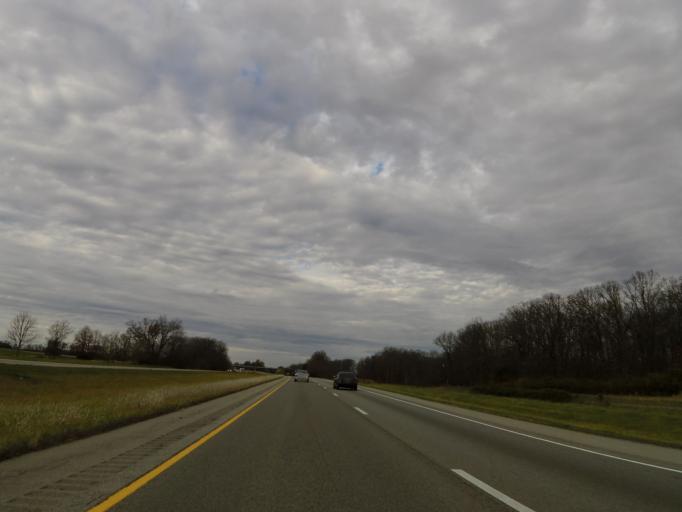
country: US
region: Illinois
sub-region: Clinton County
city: Wamac
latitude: 38.3834
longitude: -89.1201
